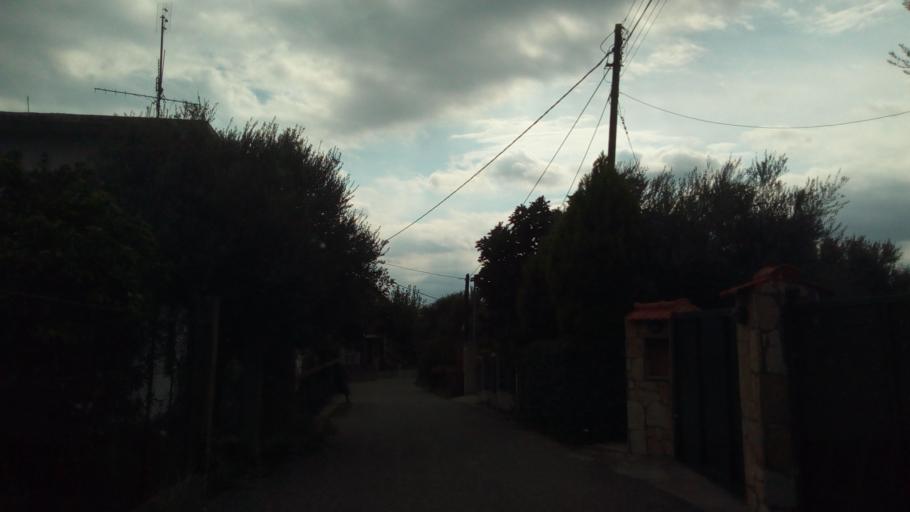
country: GR
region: West Greece
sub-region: Nomos Achaias
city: Kamarai
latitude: 38.3927
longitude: 22.0107
